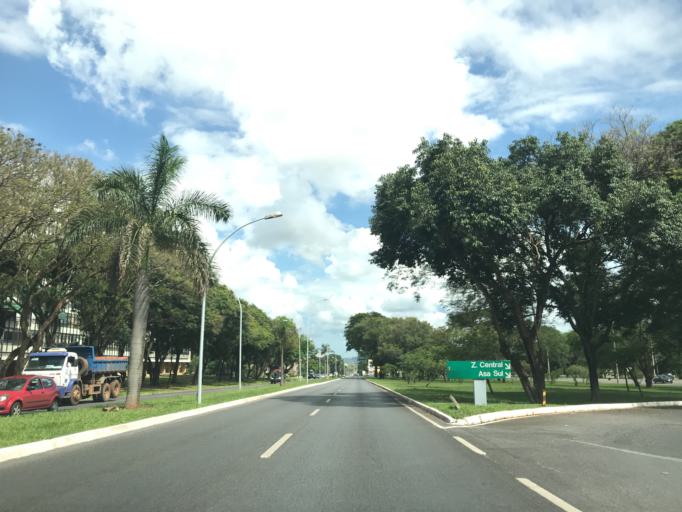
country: BR
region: Federal District
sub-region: Brasilia
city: Brasilia
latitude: -15.7634
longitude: -47.8843
